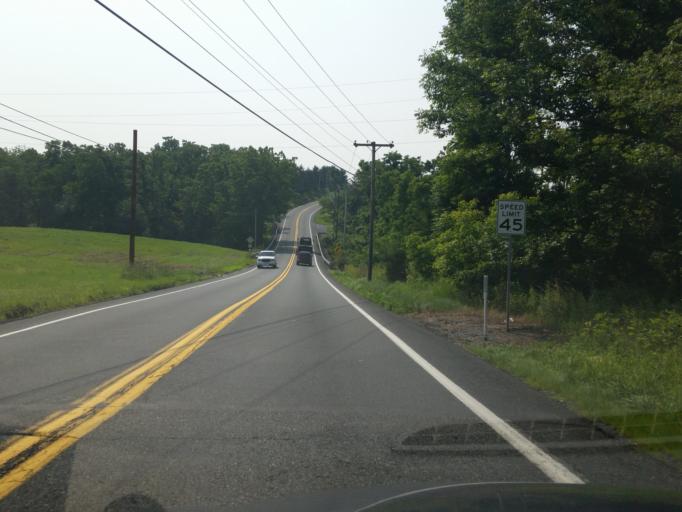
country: US
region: Pennsylvania
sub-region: Dauphin County
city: Palmdale
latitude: 40.3665
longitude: -76.6486
